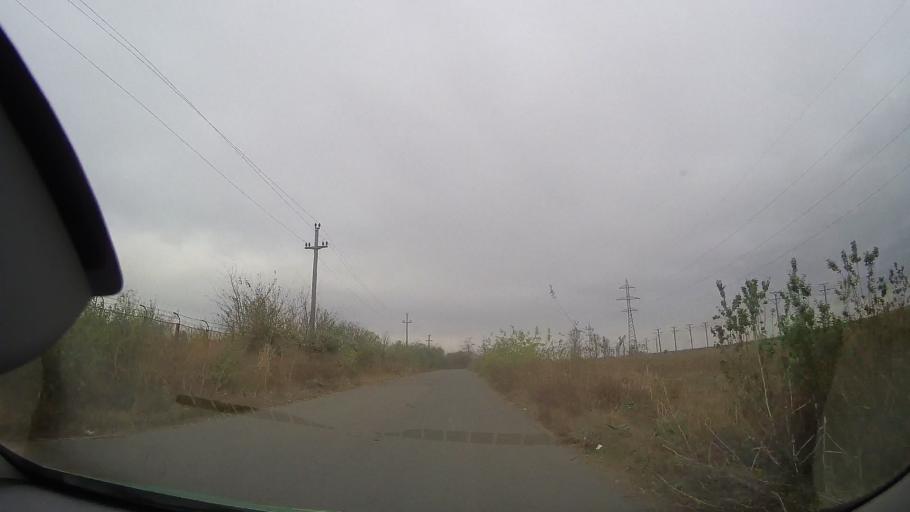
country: RO
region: Braila
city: Dudesti
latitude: 44.8953
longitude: 27.4342
